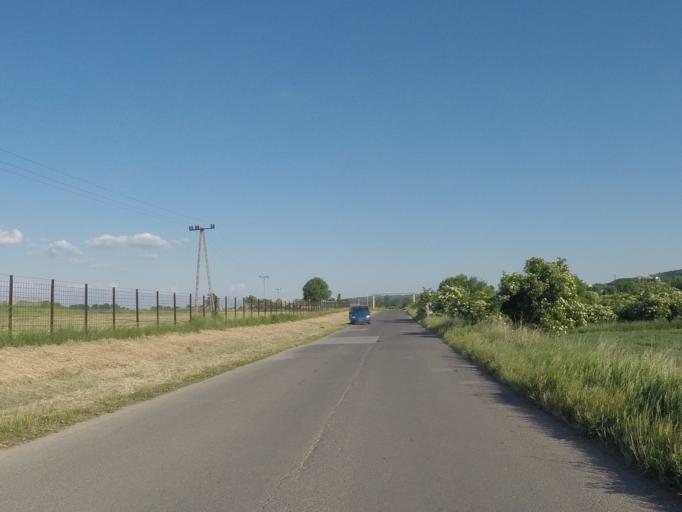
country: HU
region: Borsod-Abauj-Zemplen
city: Kazincbarcika
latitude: 48.2516
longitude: 20.6591
